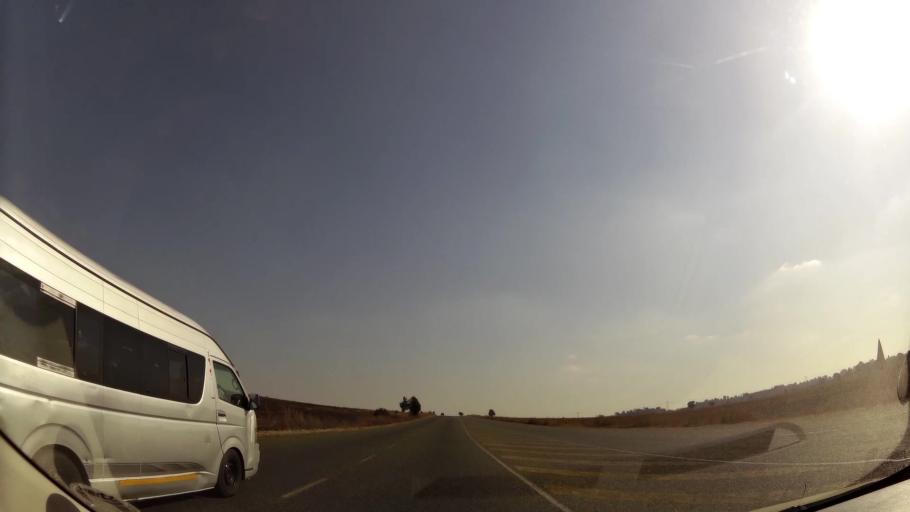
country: ZA
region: Gauteng
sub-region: West Rand District Municipality
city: Randfontein
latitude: -26.1817
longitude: 27.7484
